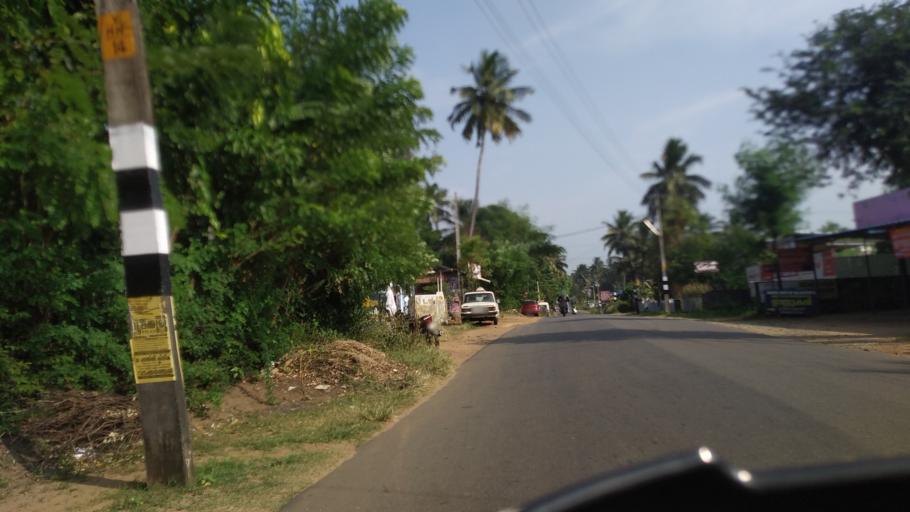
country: IN
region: Kerala
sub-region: Thrissur District
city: Chelakara
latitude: 10.6008
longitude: 76.4938
